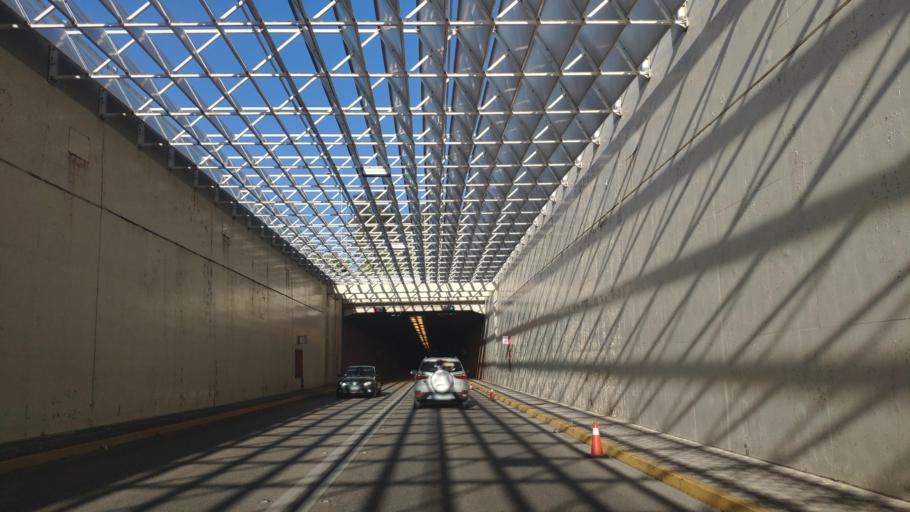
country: GR
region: Epirus
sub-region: Nomos Prevezis
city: Preveza
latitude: 38.9493
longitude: 20.7466
